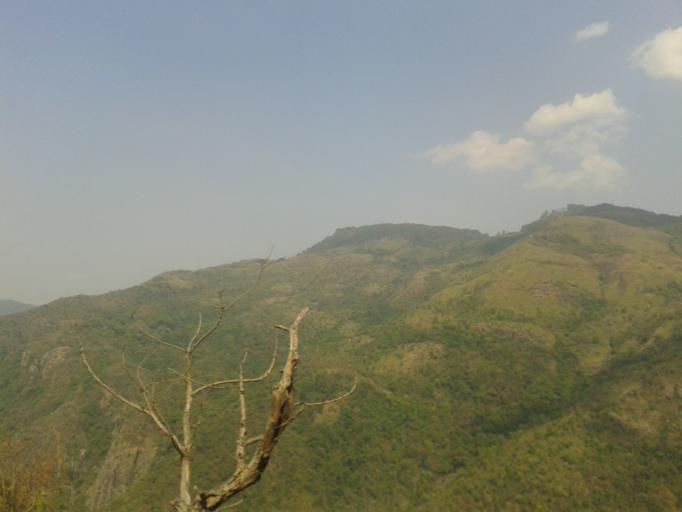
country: IN
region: Tamil Nadu
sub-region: Dindigul
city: Ayakudi
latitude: 10.3482
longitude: 77.5743
